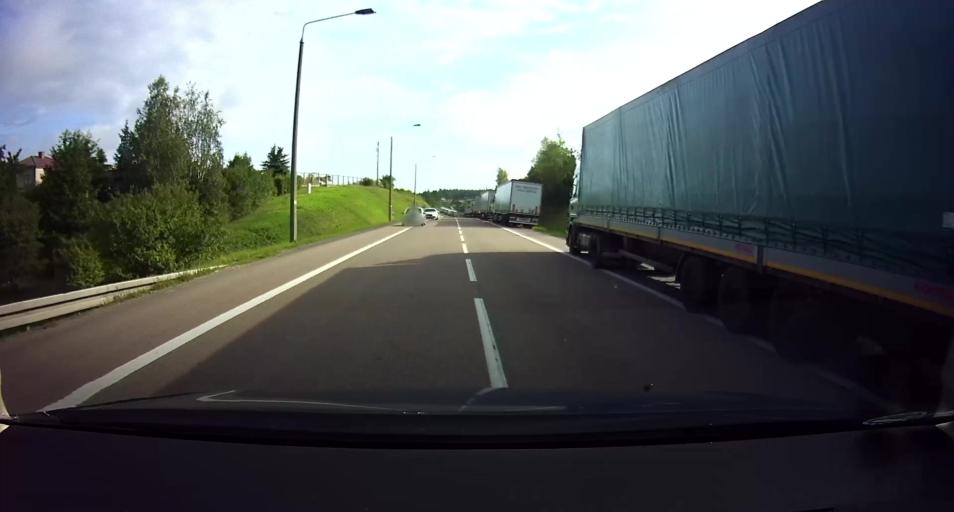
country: PL
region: Podlasie
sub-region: Powiat sokolski
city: Kuznica
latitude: 53.5087
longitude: 23.6467
